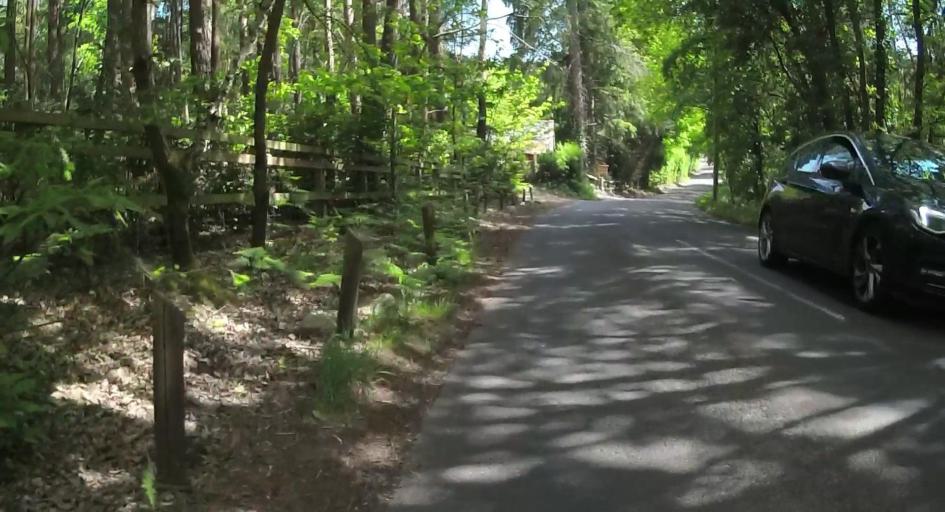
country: GB
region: England
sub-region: Surrey
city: Farnham
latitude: 51.1866
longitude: -0.8018
